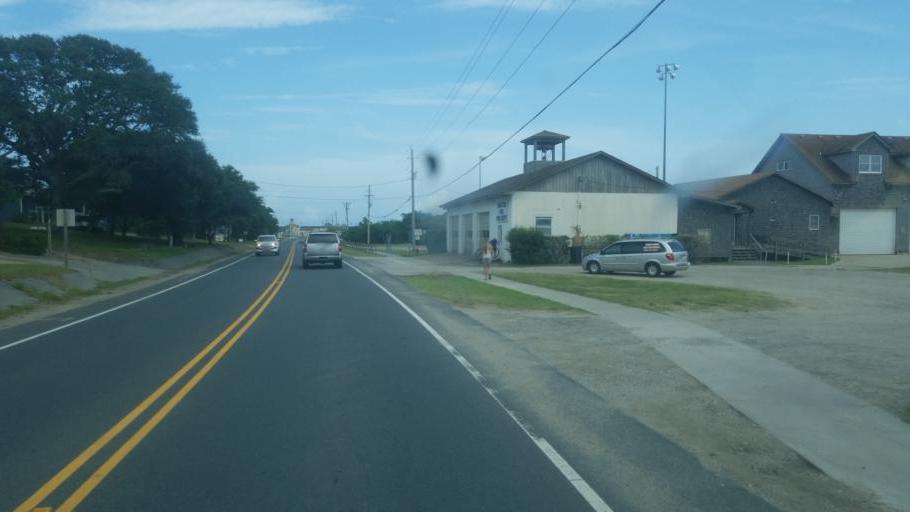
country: US
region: North Carolina
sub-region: Dare County
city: Buxton
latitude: 35.2651
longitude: -75.5278
